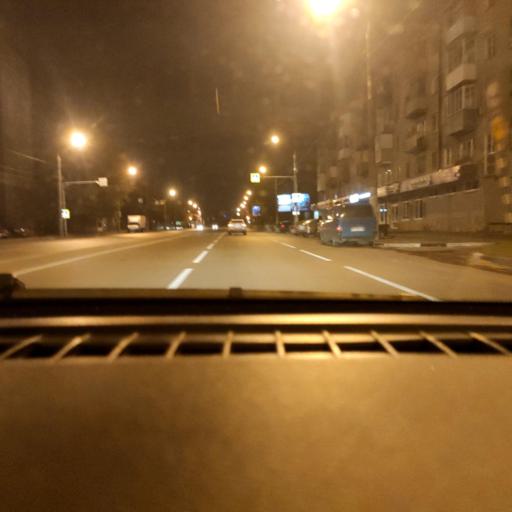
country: RU
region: Voronezj
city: Voronezh
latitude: 51.6704
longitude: 39.1615
